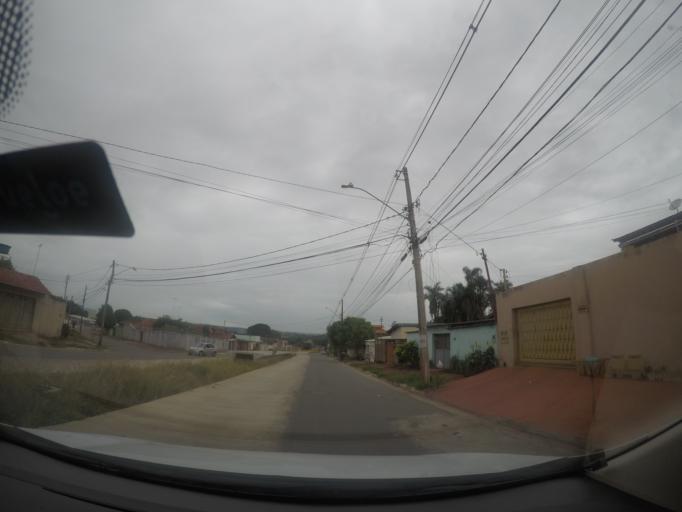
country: BR
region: Goias
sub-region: Goiania
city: Goiania
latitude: -16.6178
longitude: -49.2991
